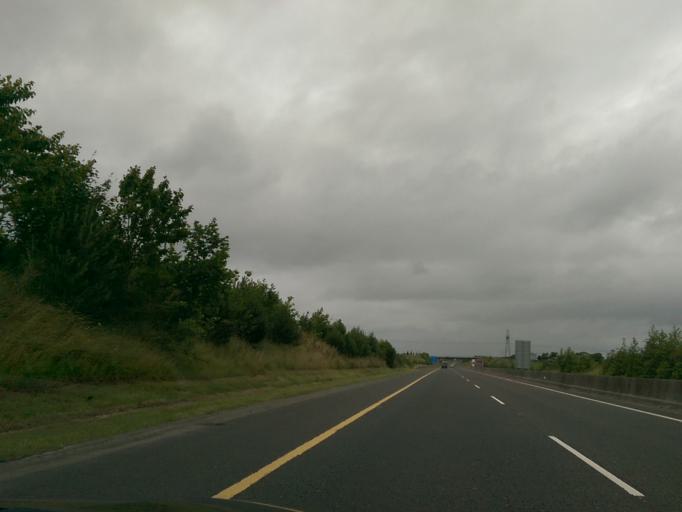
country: IE
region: Munster
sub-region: An Clar
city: Newmarket on Fergus
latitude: 52.8004
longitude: -8.9244
